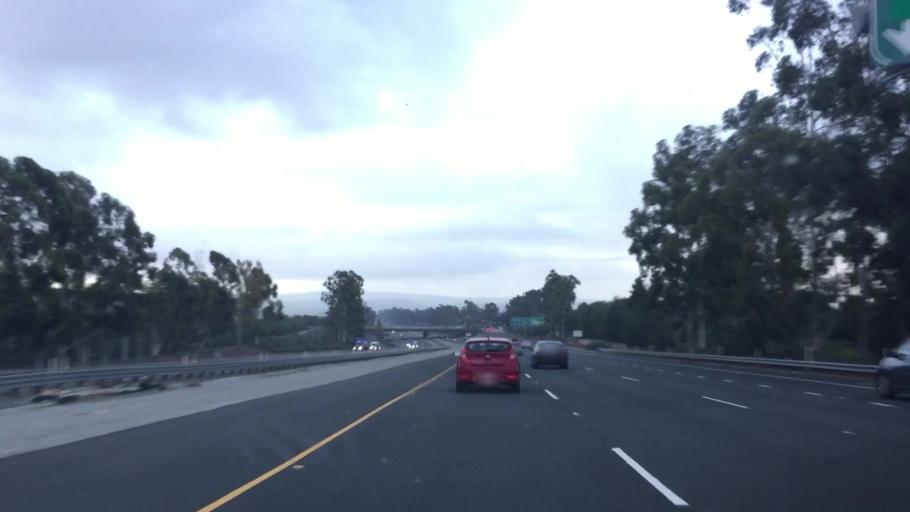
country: US
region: California
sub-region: Orange County
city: Lake Forest
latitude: 33.7022
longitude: -117.7304
